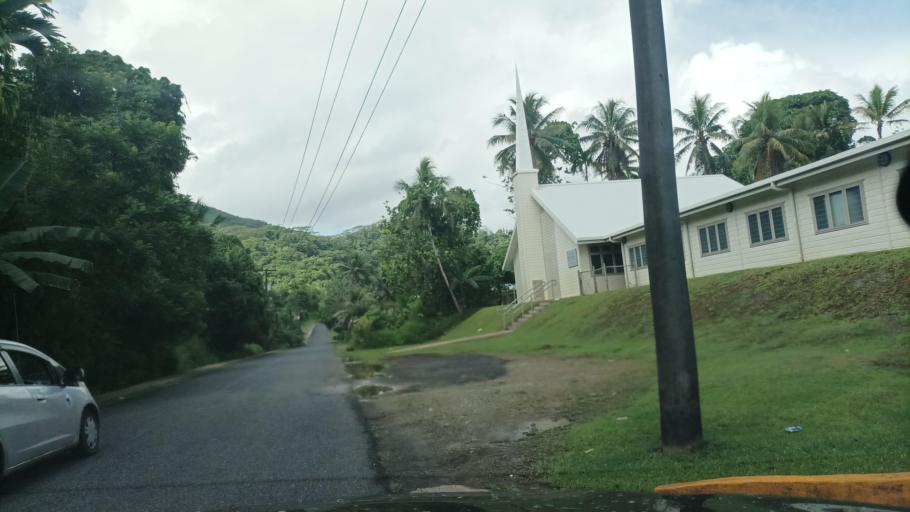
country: FM
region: Pohnpei
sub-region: Sokehs Municipality
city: Palikir - National Government Center
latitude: 6.9336
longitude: 158.1810
